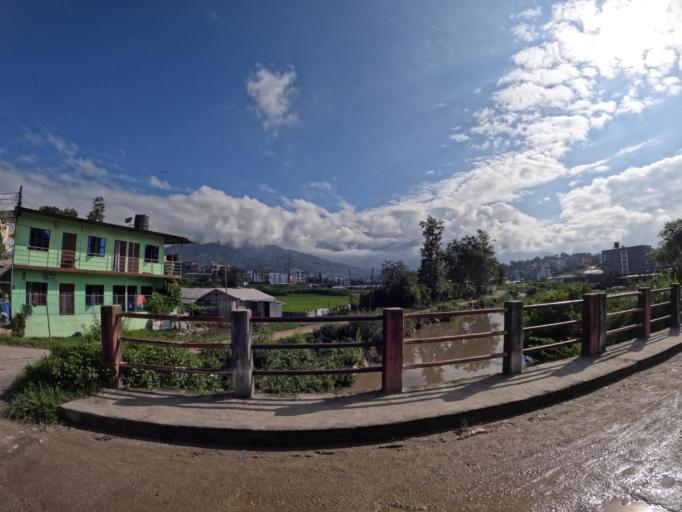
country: NP
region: Central Region
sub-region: Bagmati Zone
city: Kathmandu
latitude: 27.7591
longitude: 85.3340
